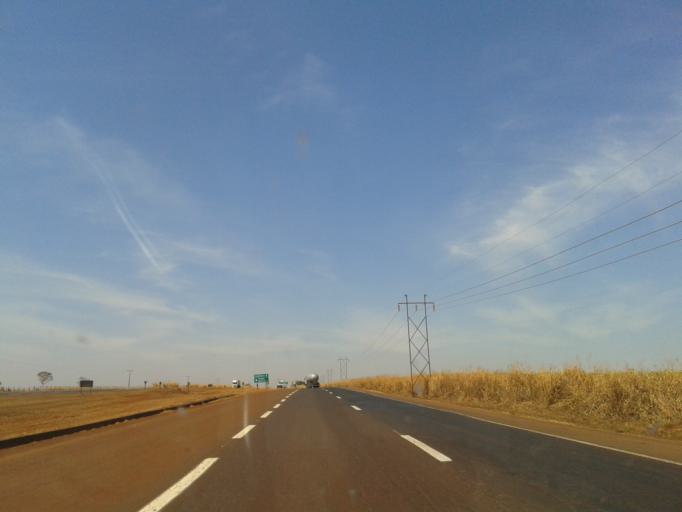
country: BR
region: Goias
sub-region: Itumbiara
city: Itumbiara
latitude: -18.2379
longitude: -49.2584
